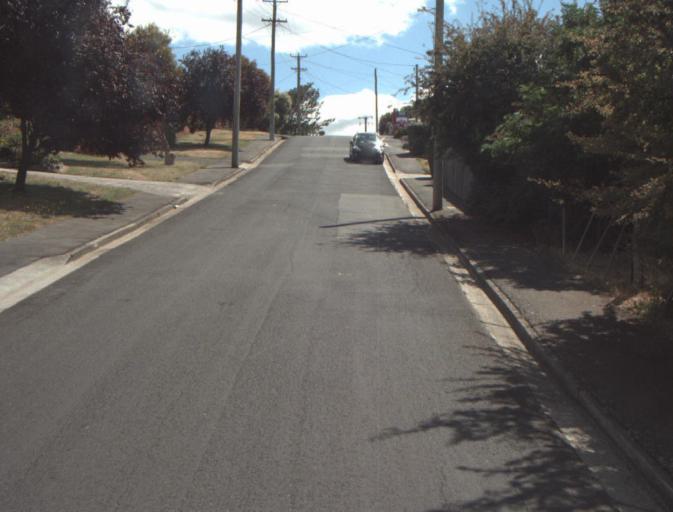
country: AU
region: Tasmania
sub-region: Launceston
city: Newnham
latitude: -41.4120
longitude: 147.1519
